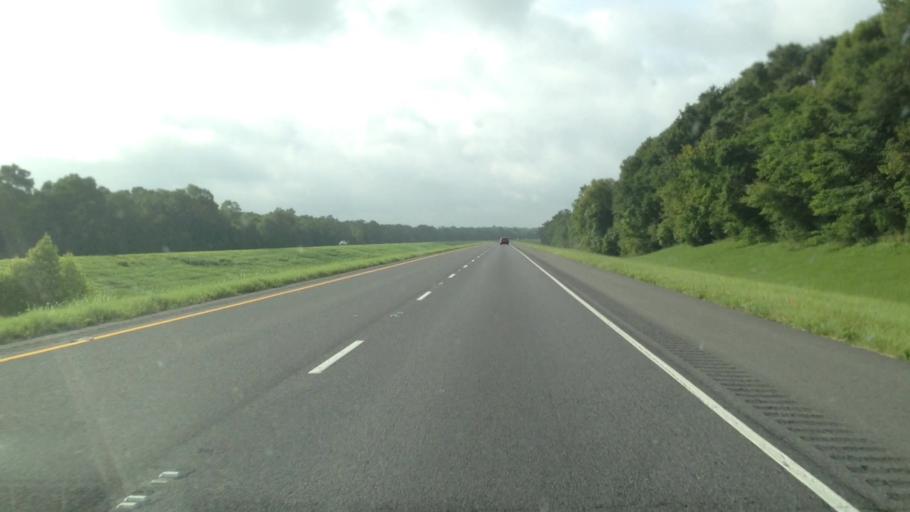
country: US
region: Louisiana
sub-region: Saint Landry Parish
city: Opelousas
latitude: 30.7016
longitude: -92.0901
